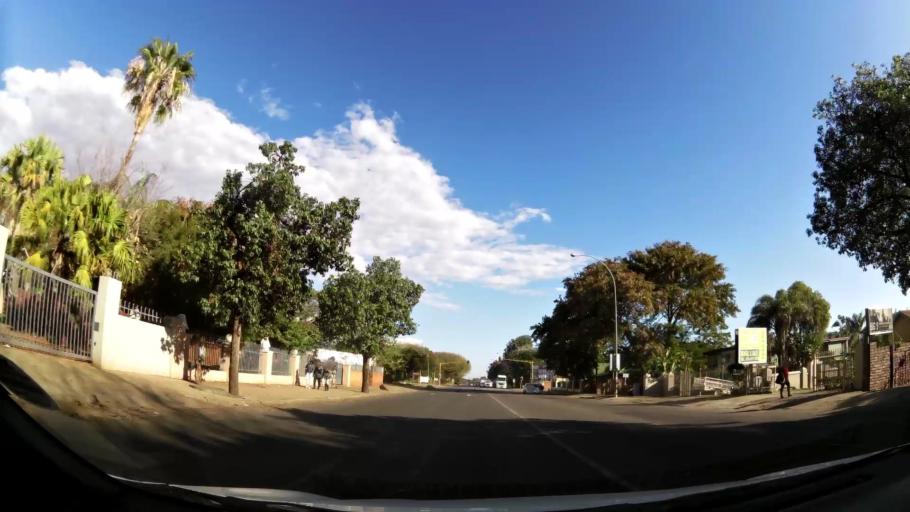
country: ZA
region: Limpopo
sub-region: Waterberg District Municipality
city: Mokopane
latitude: -24.1934
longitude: 29.0093
